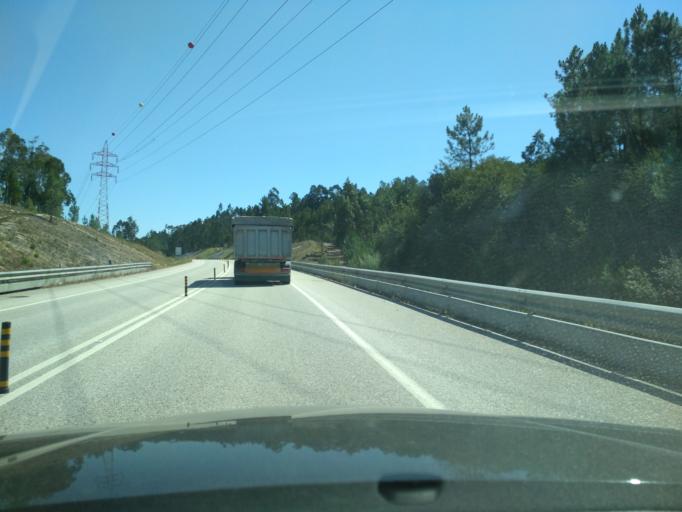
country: PT
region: Leiria
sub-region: Pombal
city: Lourical
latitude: 39.9568
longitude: -8.6915
